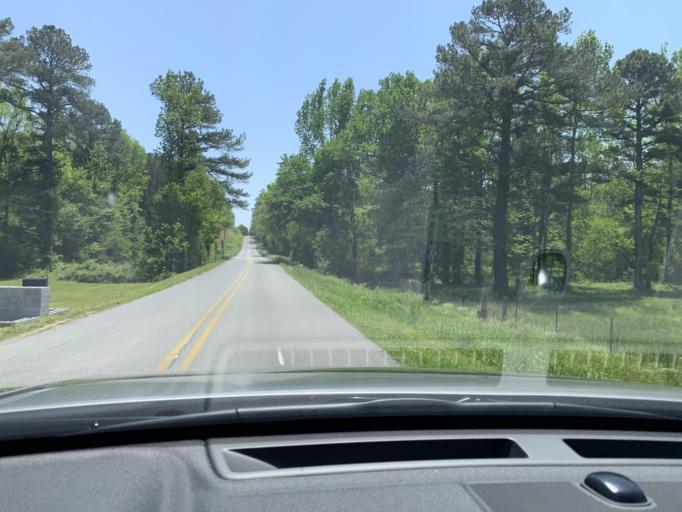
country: US
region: Georgia
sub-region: Polk County
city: Aragon
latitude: 34.0818
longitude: -85.1186
